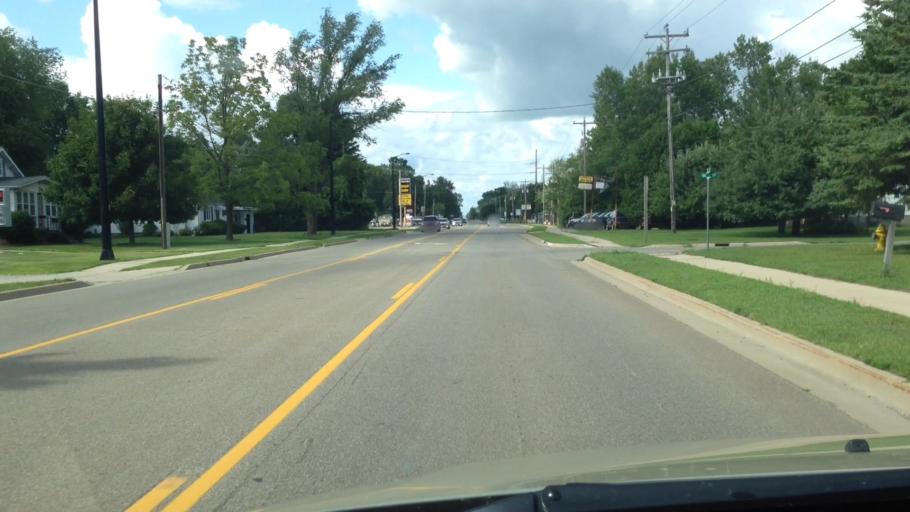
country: US
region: Michigan
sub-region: Menominee County
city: Menominee
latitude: 45.1420
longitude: -87.6121
